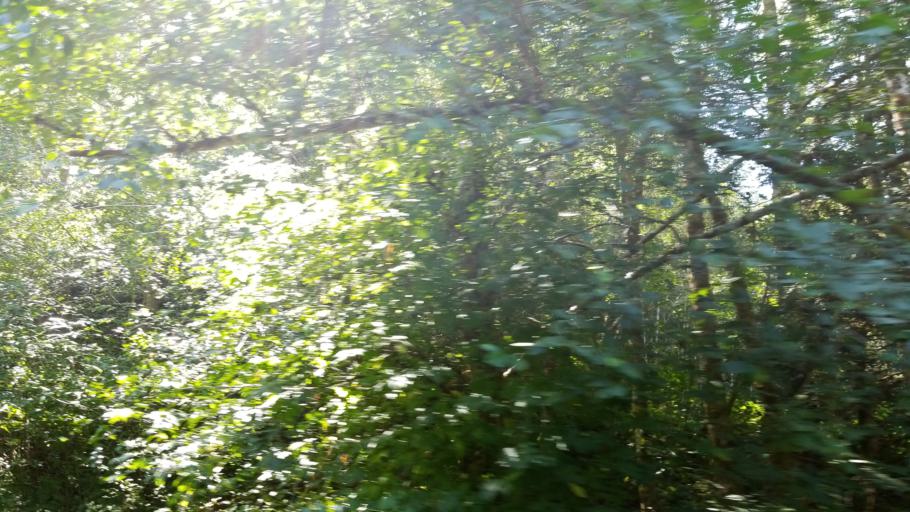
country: US
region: California
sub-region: Mendocino County
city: Fort Bragg
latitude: 39.4488
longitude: -123.7749
